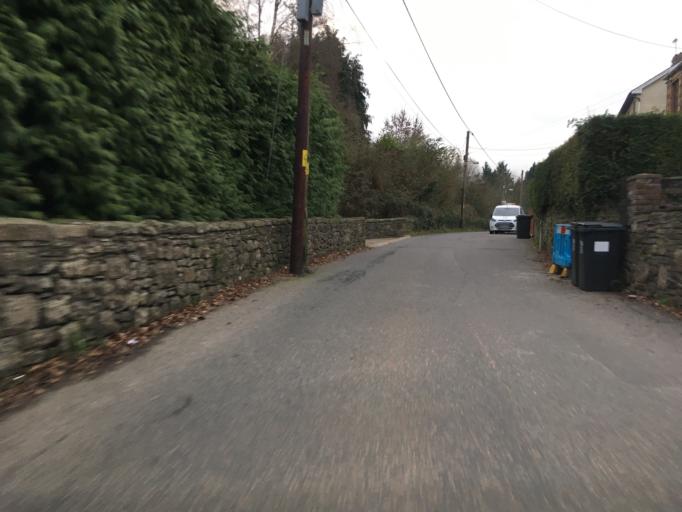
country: GB
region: Wales
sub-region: Newport
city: Marshfield
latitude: 51.5760
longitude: -3.0540
